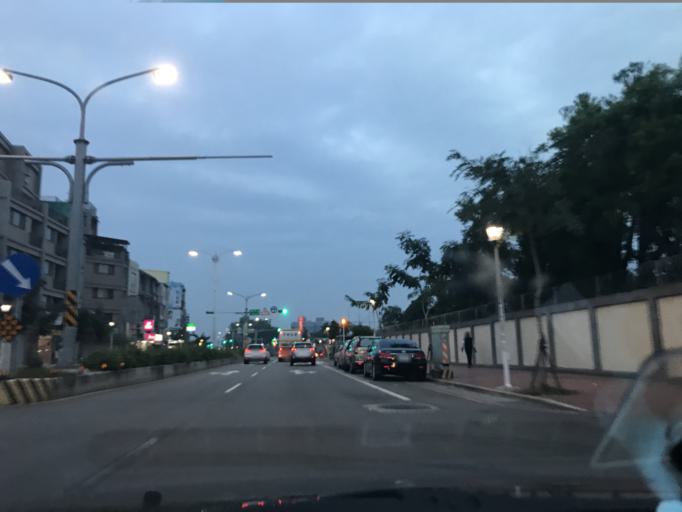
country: TW
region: Taiwan
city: Daxi
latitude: 24.9277
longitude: 121.2424
